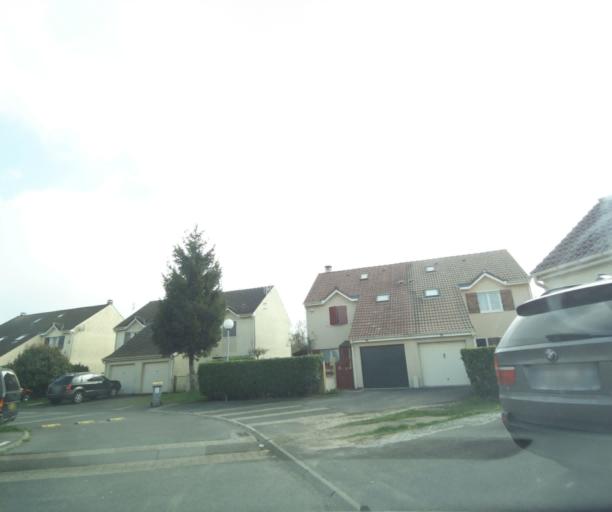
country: FR
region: Ile-de-France
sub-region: Departement du Val-d'Oise
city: Vaureal
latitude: 49.0459
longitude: 2.0199
